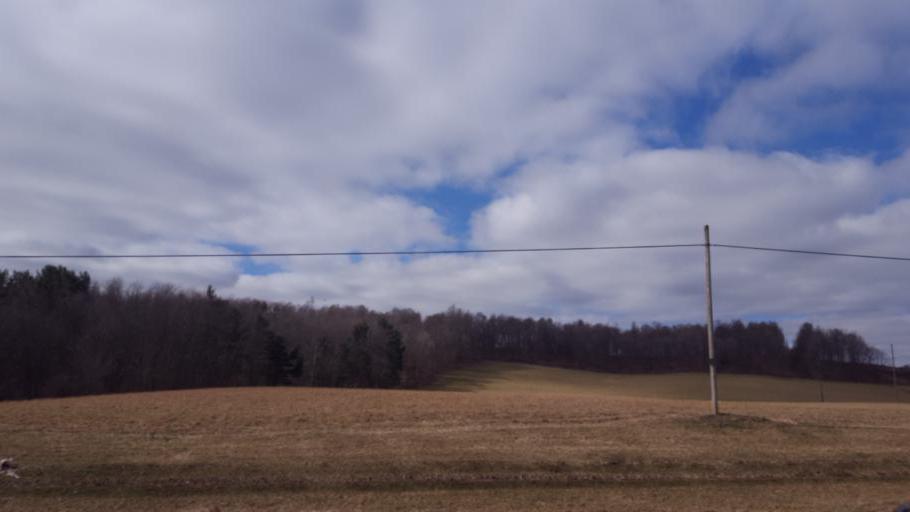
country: US
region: Ohio
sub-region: Sandusky County
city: Bellville
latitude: 40.6284
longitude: -82.5210
